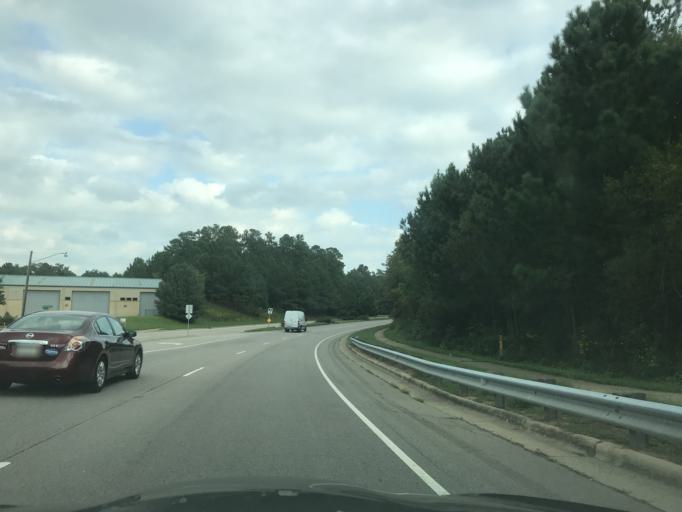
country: US
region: North Carolina
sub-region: Durham County
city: Durham
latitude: 35.9386
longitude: -78.9022
